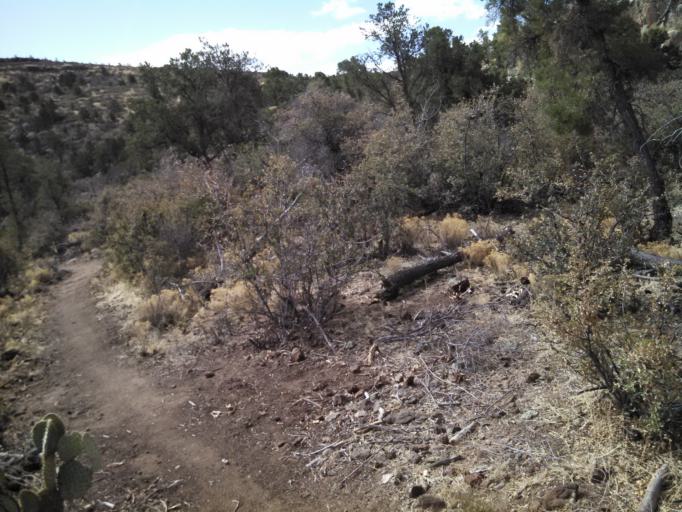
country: US
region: Arizona
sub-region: Yavapai County
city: Prescott Valley
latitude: 34.5905
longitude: -112.3975
